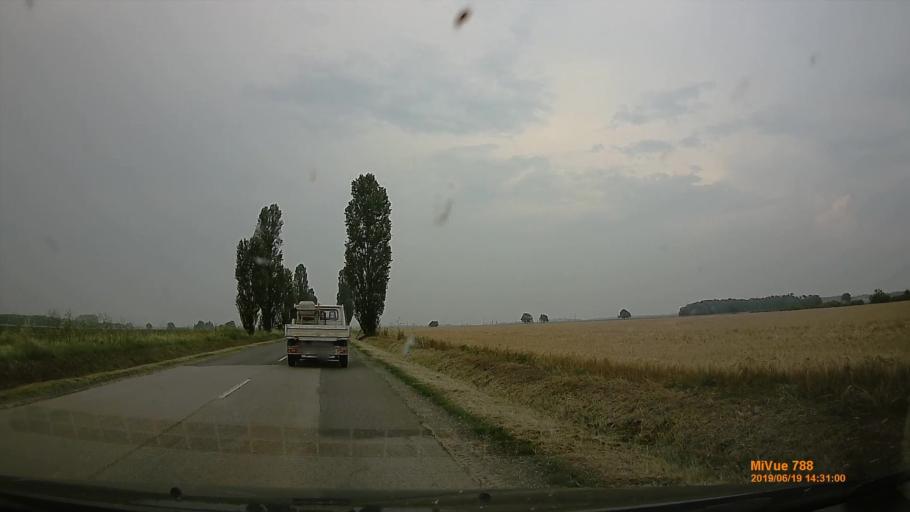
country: HU
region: Baranya
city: Szigetvar
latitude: 46.0681
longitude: 17.7688
